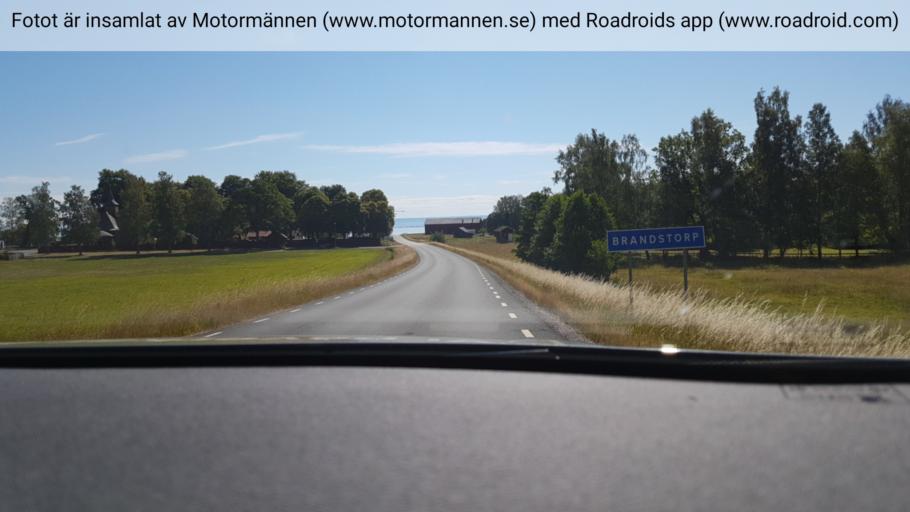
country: SE
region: Joenkoeping
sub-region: Habo Kommun
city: Habo
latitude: 58.1014
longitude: 14.1813
